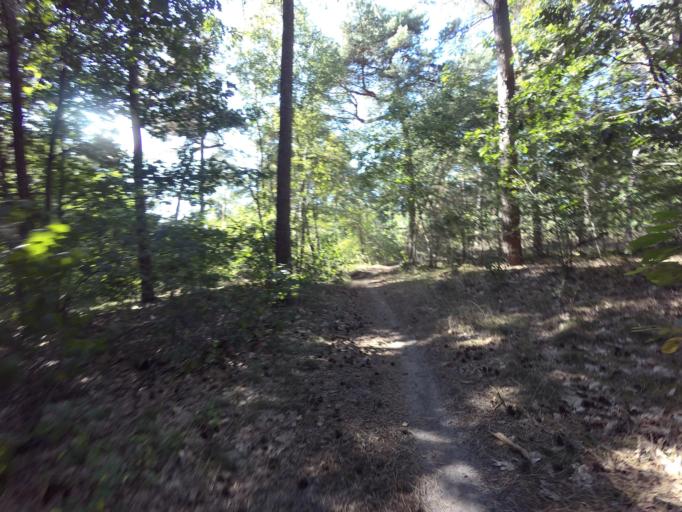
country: NL
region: North Brabant
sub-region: Gemeente Someren
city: Someren
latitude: 51.3629
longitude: 5.6531
